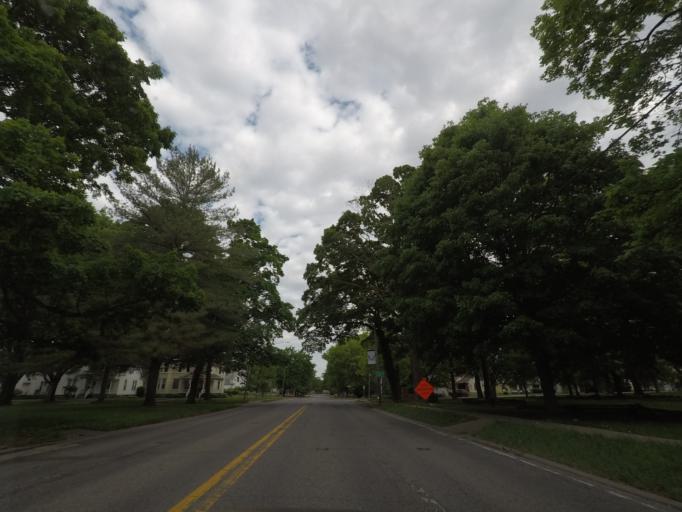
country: US
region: Illinois
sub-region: Logan County
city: Lincoln
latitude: 40.1551
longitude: -89.3624
